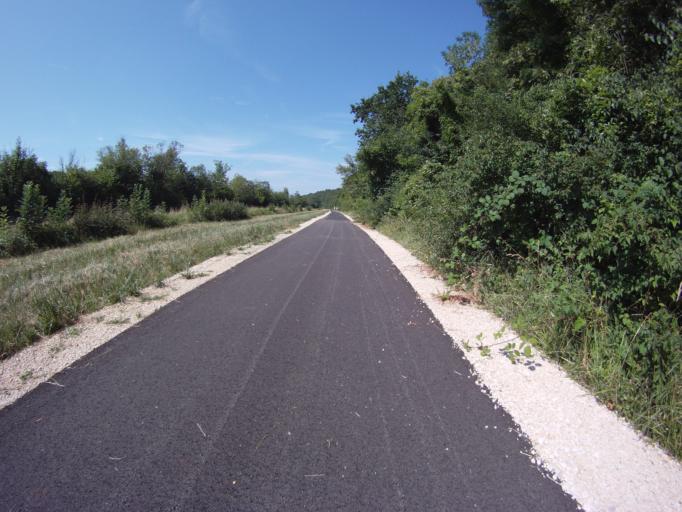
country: FR
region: Lorraine
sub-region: Departement de Meurthe-et-Moselle
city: Villey-Saint-Etienne
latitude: 48.7542
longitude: 6.0168
